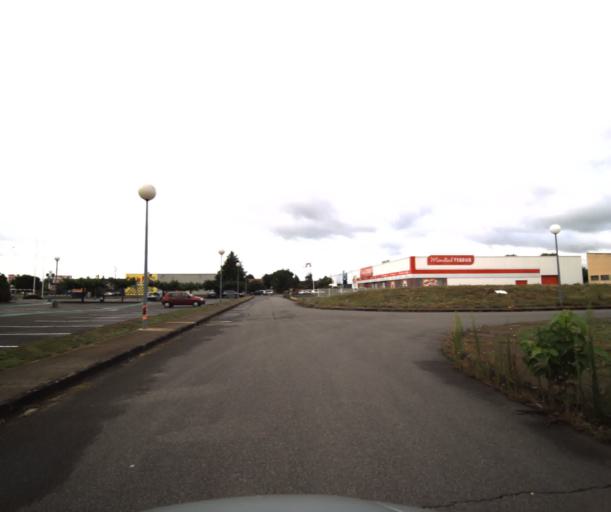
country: FR
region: Midi-Pyrenees
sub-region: Departement de la Haute-Garonne
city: Portet-sur-Garonne
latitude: 43.5381
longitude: 1.4102
